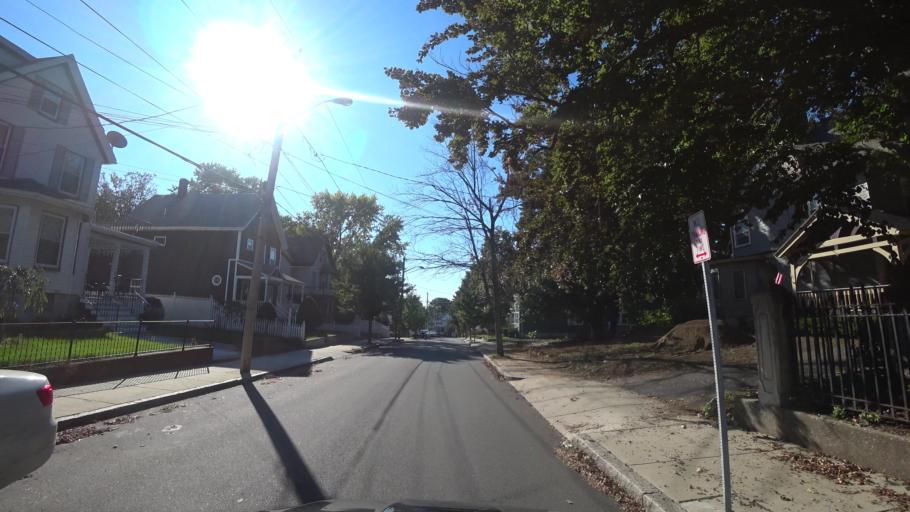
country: US
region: Massachusetts
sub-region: Middlesex County
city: Malden
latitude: 42.4180
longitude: -71.0627
